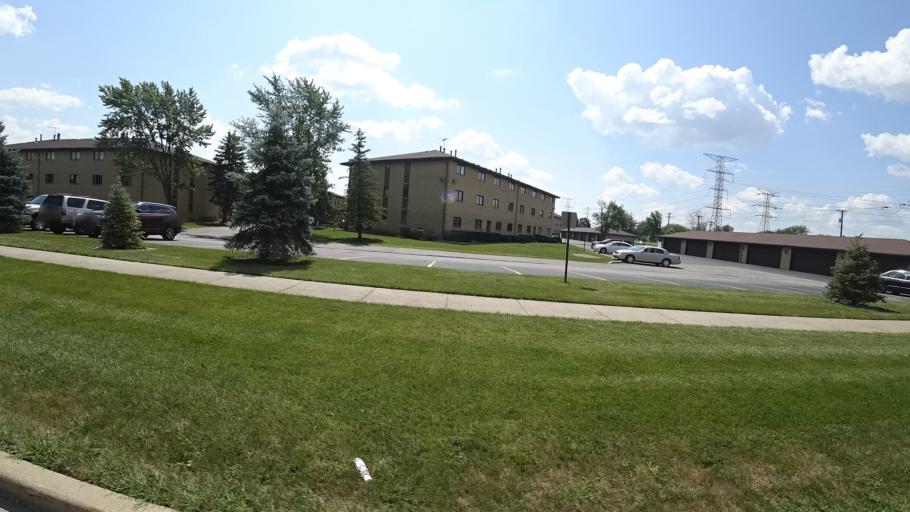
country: US
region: Illinois
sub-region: Cook County
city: Tinley Park
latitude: 41.6169
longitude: -87.7980
